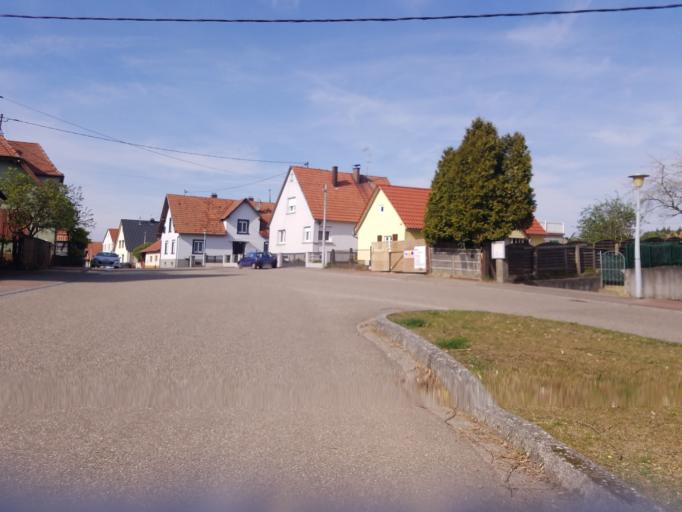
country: FR
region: Alsace
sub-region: Departement du Bas-Rhin
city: Betschdorf
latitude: 48.9009
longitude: 7.9552
